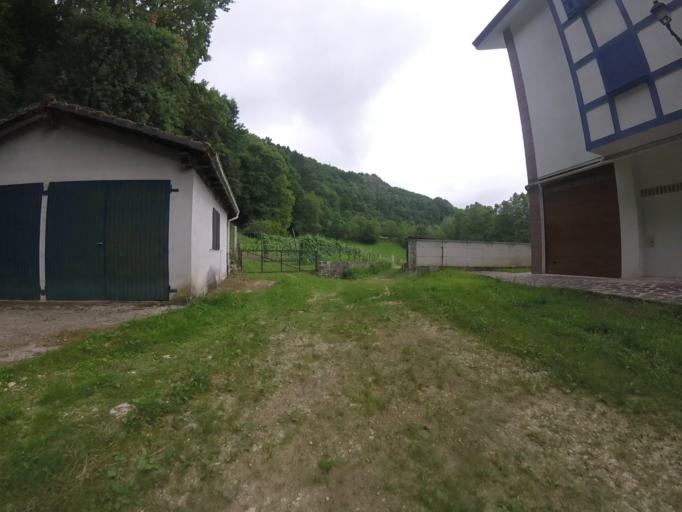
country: ES
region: Navarre
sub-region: Provincia de Navarra
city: Sunbilla
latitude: 43.1664
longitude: -1.6758
